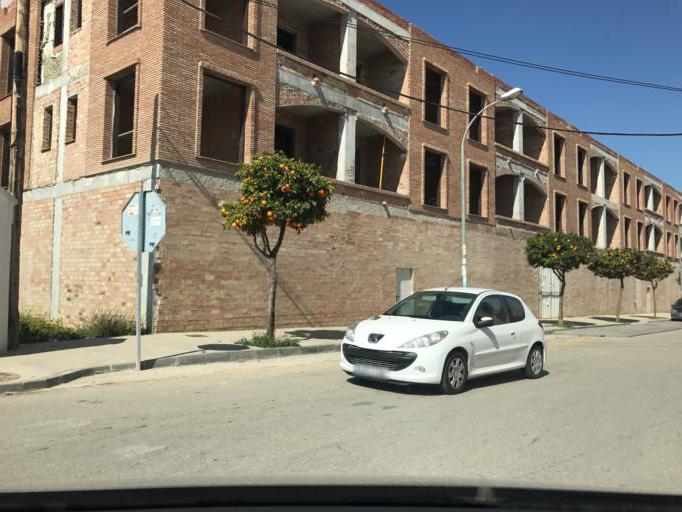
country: ES
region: Andalusia
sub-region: Provincia de Granada
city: Cijuela
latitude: 37.1953
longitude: -3.8109
